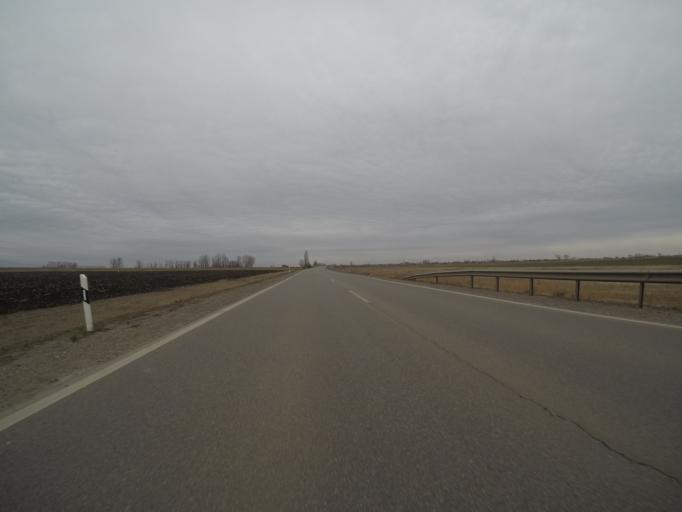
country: HU
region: Jasz-Nagykun-Szolnok
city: Jaszjakohalma
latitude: 47.5189
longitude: 19.9622
